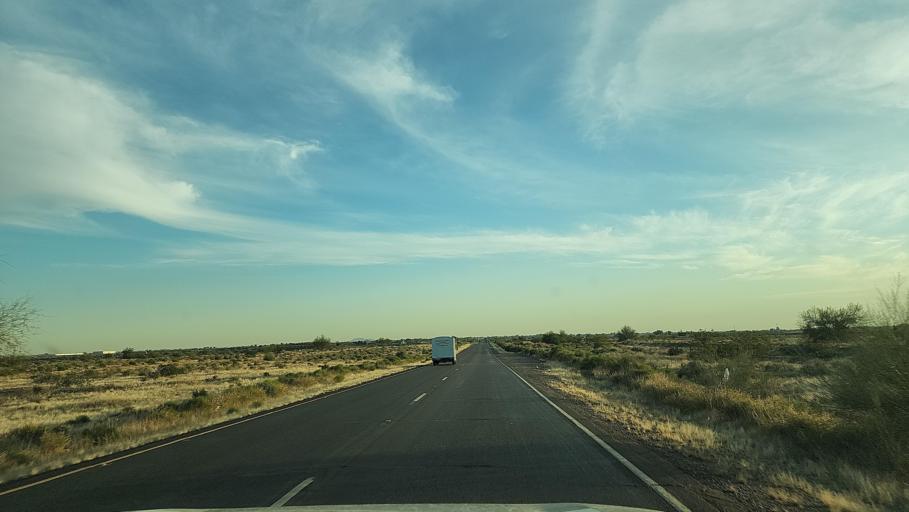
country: US
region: Arizona
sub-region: Maricopa County
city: Mesa
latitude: 33.4968
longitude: -111.7875
